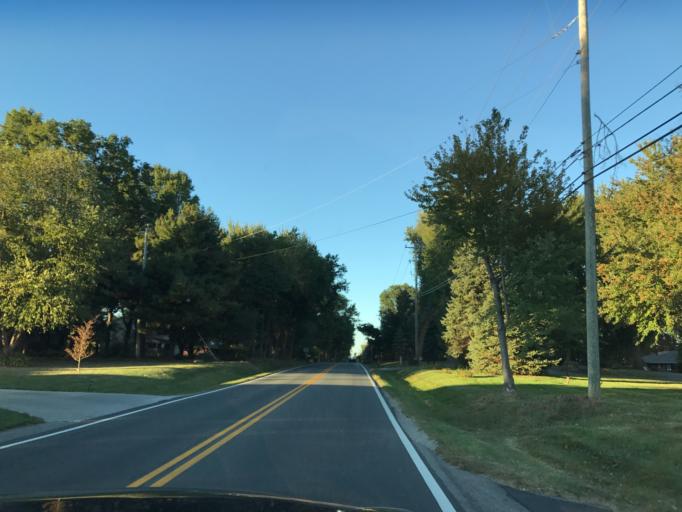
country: US
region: Ohio
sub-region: Franklin County
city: Westerville
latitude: 40.1483
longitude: -82.8827
